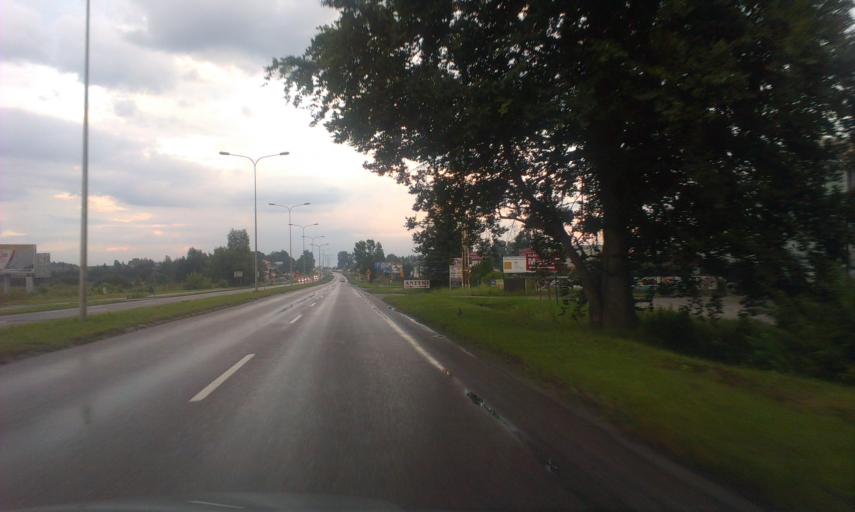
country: PL
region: West Pomeranian Voivodeship
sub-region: Koszalin
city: Koszalin
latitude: 54.1669
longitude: 16.2118
